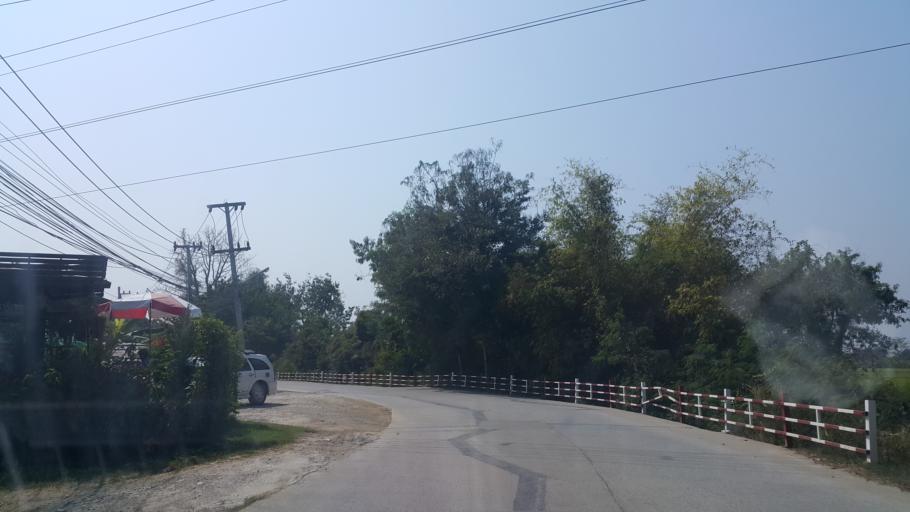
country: TH
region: Chiang Mai
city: Saraphi
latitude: 18.7367
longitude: 99.0741
